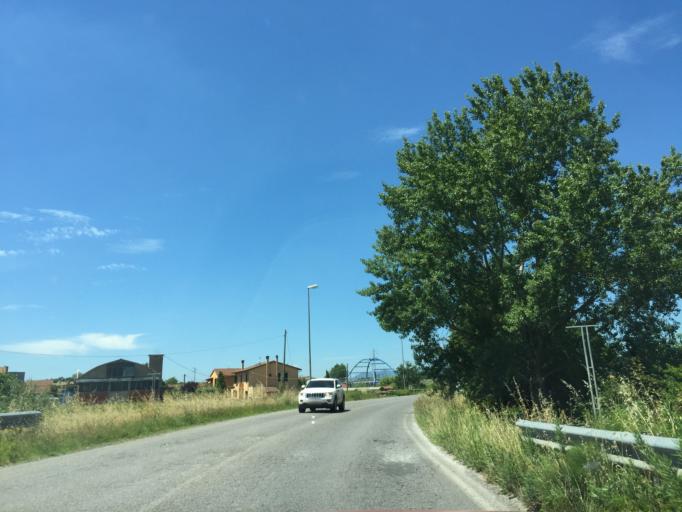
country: IT
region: Tuscany
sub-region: Province of Pisa
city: San Miniato
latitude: 43.6900
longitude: 10.8032
